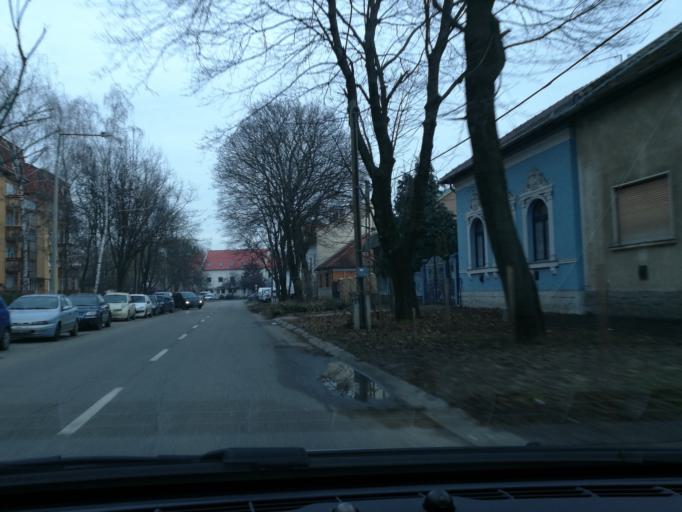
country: HU
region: Szabolcs-Szatmar-Bereg
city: Nyiregyhaza
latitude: 47.9483
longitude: 21.7301
